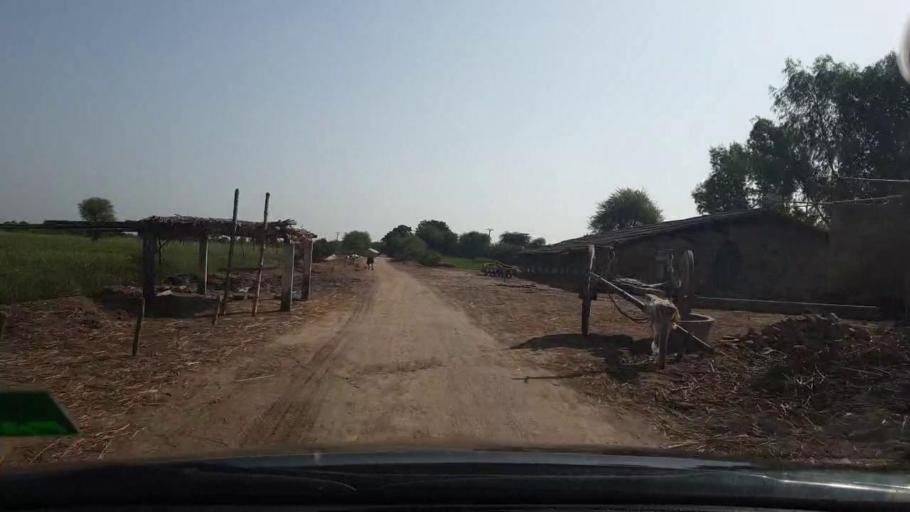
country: PK
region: Sindh
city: Tando Bago
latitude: 24.7204
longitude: 68.9931
